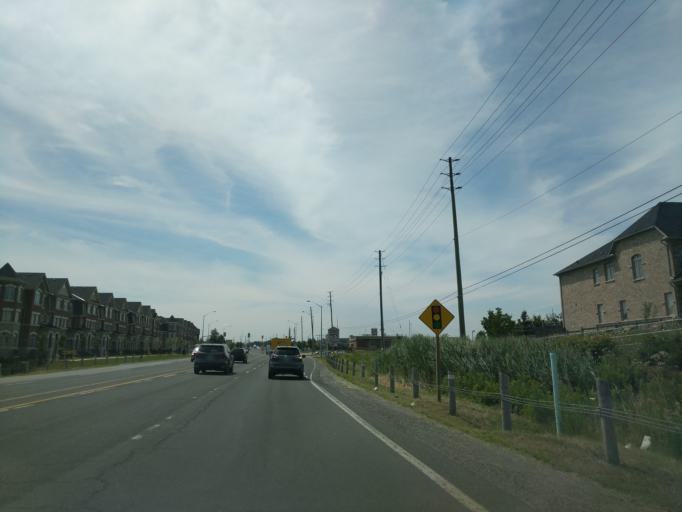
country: CA
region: Ontario
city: Vaughan
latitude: 43.8627
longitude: -79.4807
